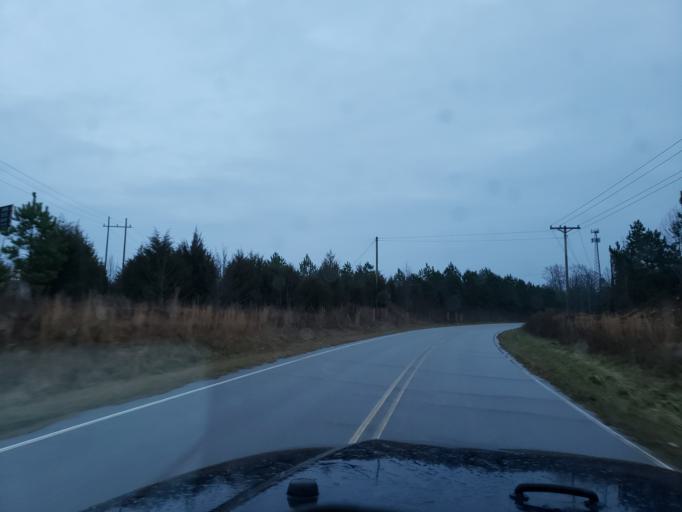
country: US
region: South Carolina
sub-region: Cherokee County
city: Blacksburg
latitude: 35.1581
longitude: -81.4669
